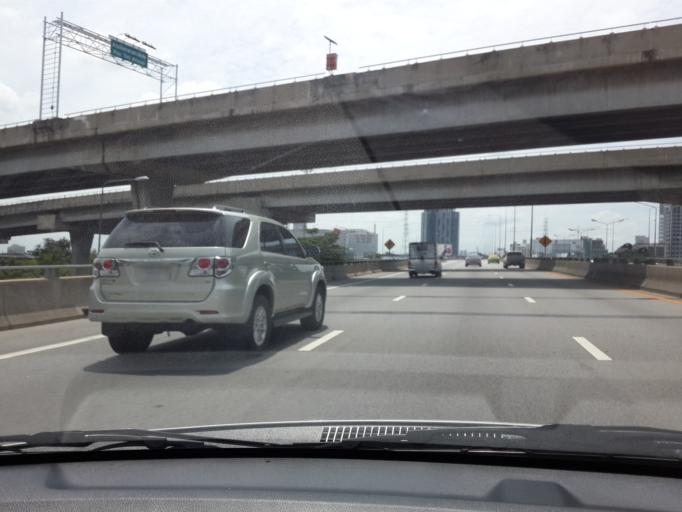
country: TH
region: Bangkok
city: Watthana
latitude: 13.7514
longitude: 100.5940
